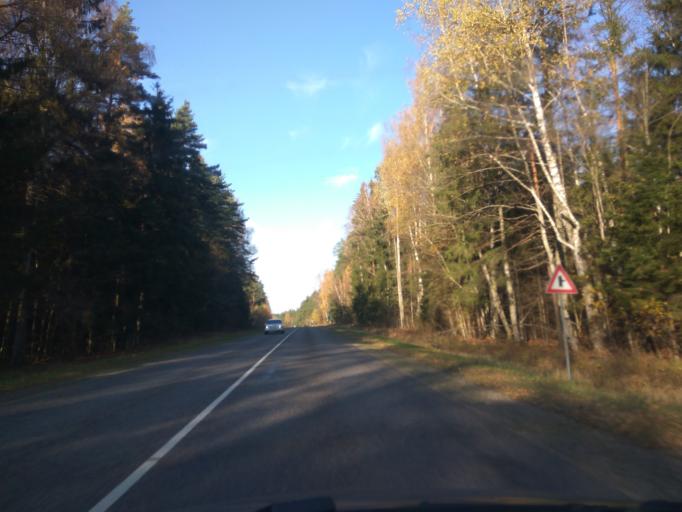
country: LV
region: Kuldigas Rajons
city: Kuldiga
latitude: 57.0601
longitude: 21.8142
